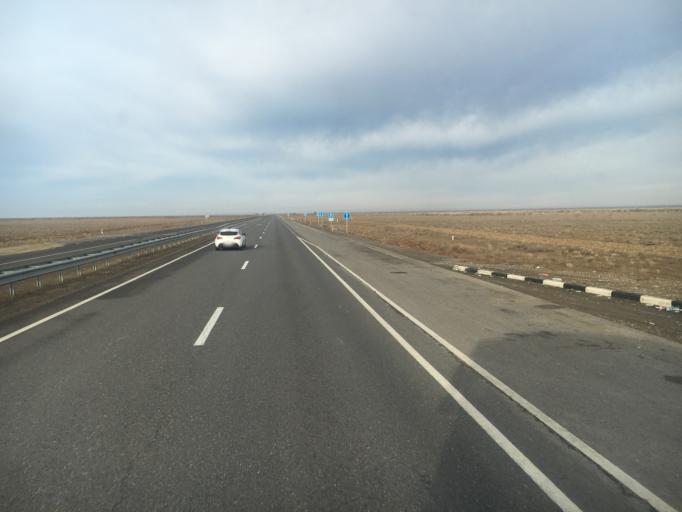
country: KZ
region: Ongtustik Qazaqstan
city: Turkestan
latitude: 43.5169
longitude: 67.8122
